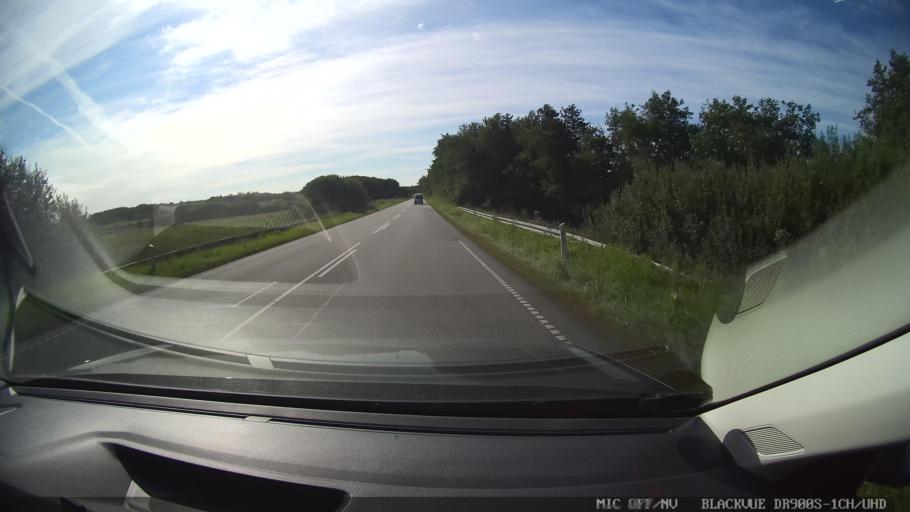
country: DK
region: North Denmark
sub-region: Mariagerfjord Kommune
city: Hadsund
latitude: 56.7438
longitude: 10.0756
